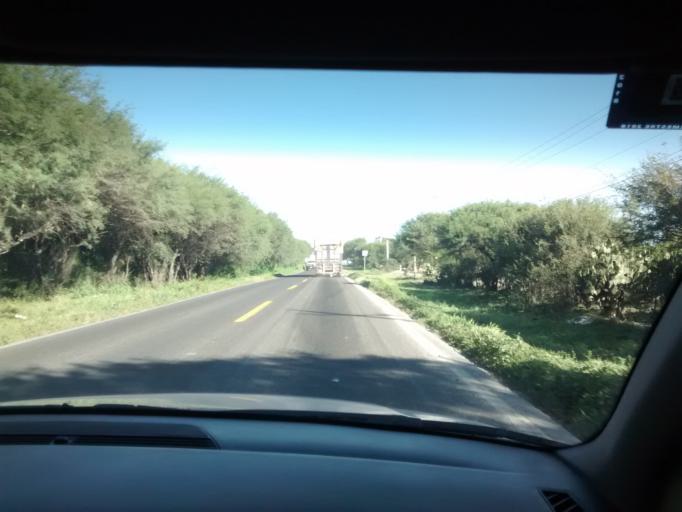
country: MX
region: Puebla
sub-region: Tepanco de Lopez
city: San Andres Cacaloapan
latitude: 18.5500
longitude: -97.5508
